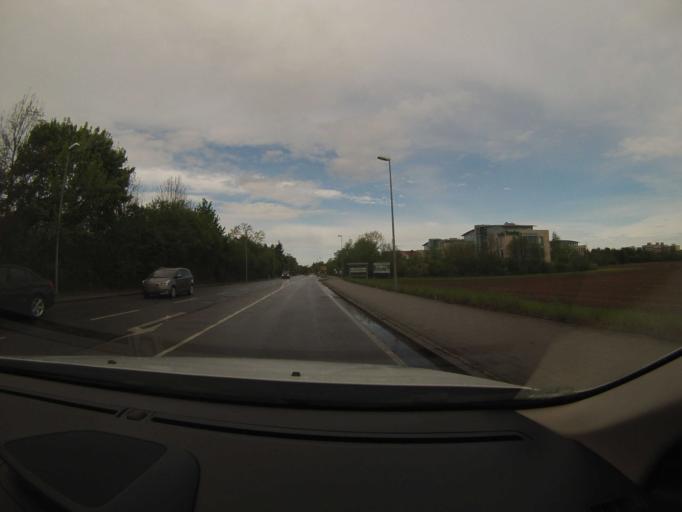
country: DE
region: Bavaria
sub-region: Upper Bavaria
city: Unterhaching
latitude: 48.0599
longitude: 11.6325
